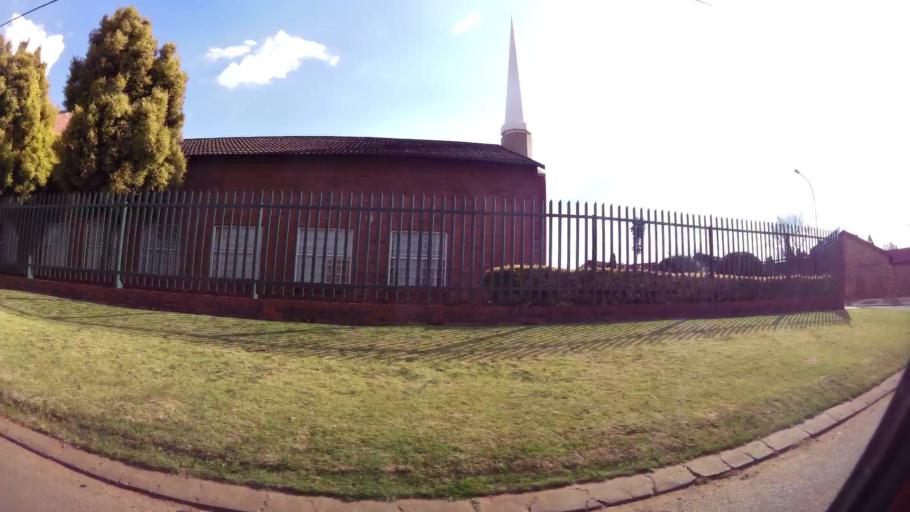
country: ZA
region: Gauteng
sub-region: City of Johannesburg Metropolitan Municipality
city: Roodepoort
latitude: -26.2115
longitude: 27.8681
